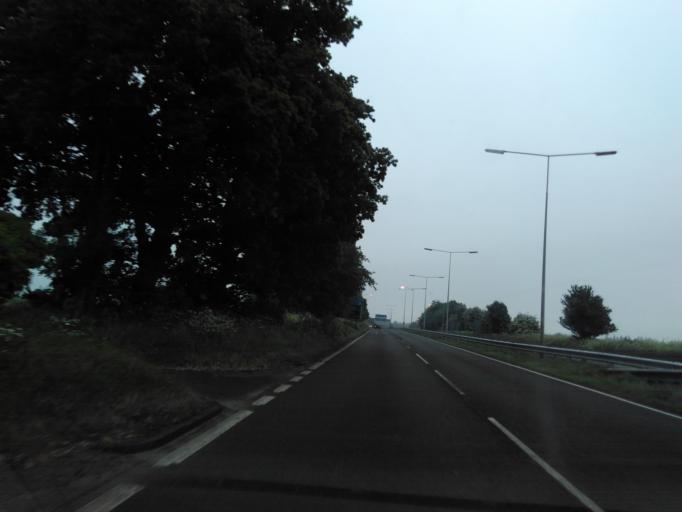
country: GB
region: England
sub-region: Kent
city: Faversham
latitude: 51.3058
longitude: 0.9305
